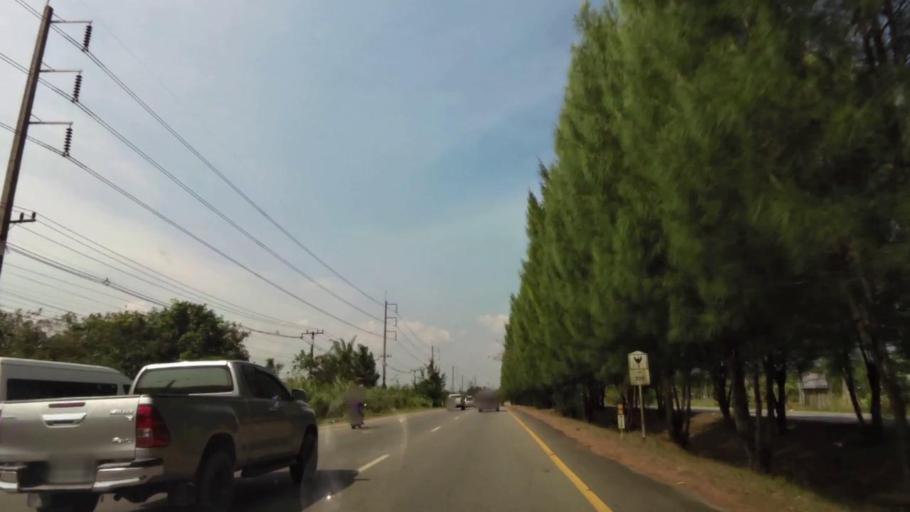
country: TH
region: Chanthaburi
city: Chanthaburi
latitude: 12.6584
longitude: 102.1234
